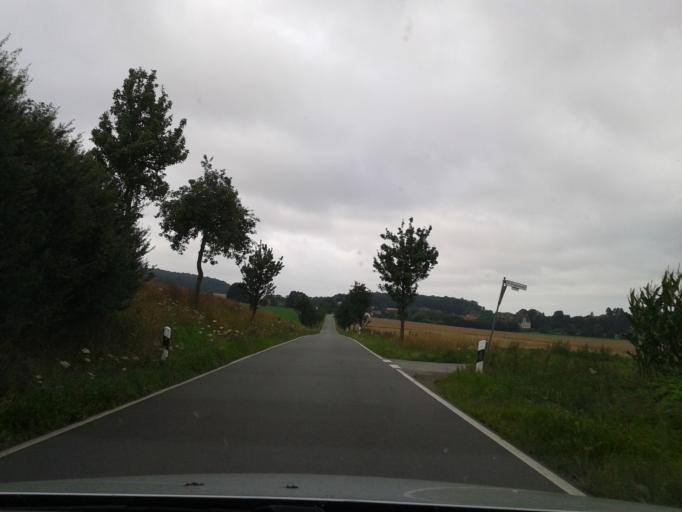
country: DE
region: North Rhine-Westphalia
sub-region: Regierungsbezirk Detmold
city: Dorentrup
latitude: 52.0137
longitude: 9.0342
